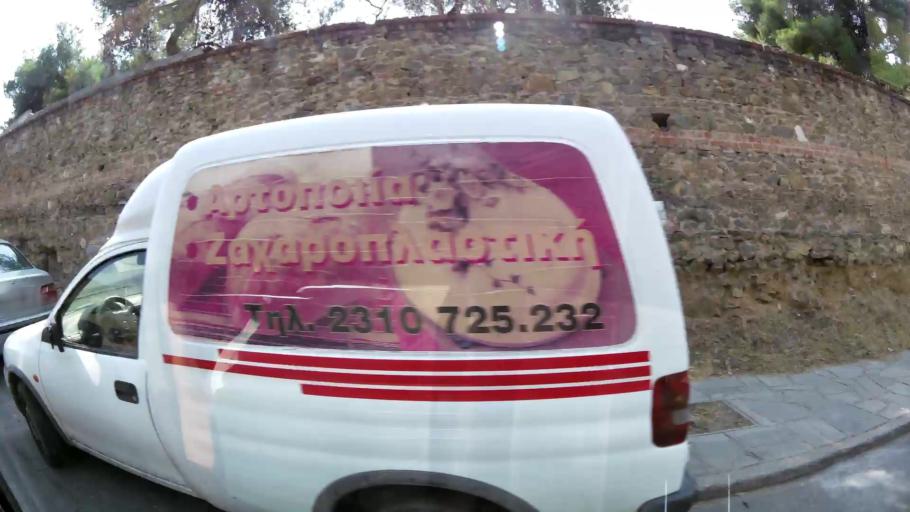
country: GR
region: Central Macedonia
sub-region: Nomos Thessalonikis
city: Agios Pavlos
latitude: 40.6378
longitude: 22.9578
